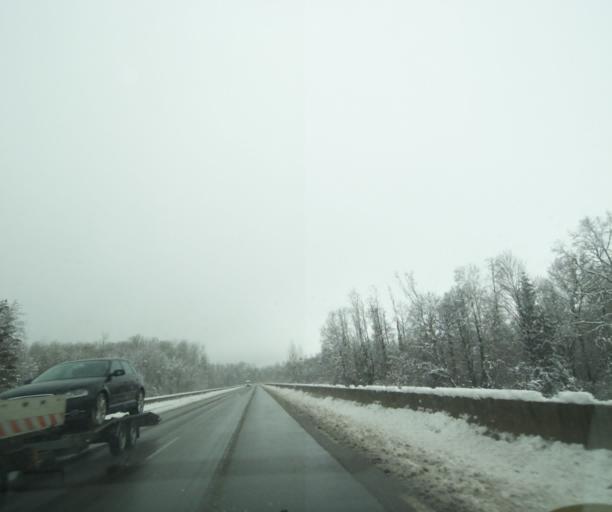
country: FR
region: Champagne-Ardenne
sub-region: Departement de la Haute-Marne
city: Villiers-en-Lieu
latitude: 48.5776
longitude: 4.8655
